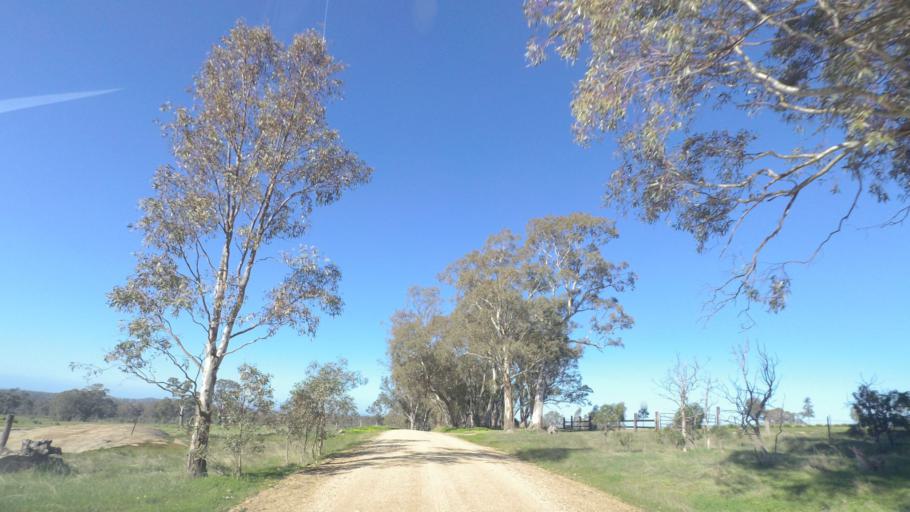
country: AU
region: Victoria
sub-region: Mount Alexander
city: Castlemaine
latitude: -36.9640
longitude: 144.3417
